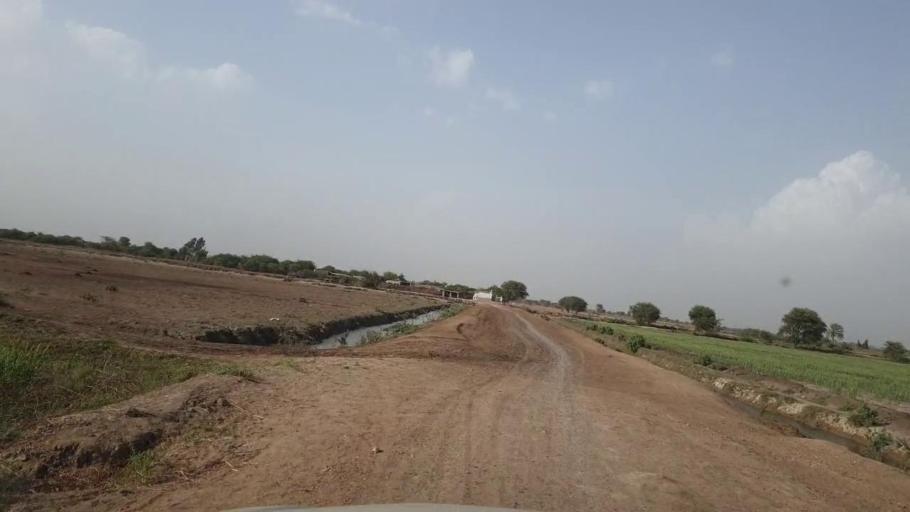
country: PK
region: Sindh
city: Tando Ghulam Ali
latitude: 25.1064
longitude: 68.8619
